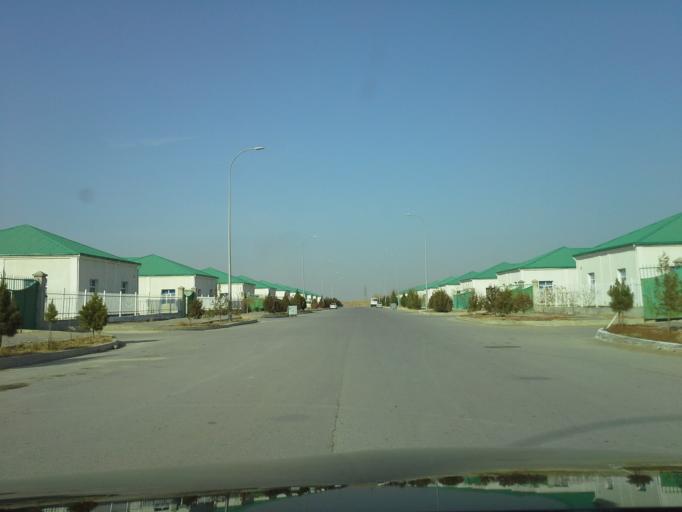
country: TM
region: Ahal
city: Abadan
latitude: 38.1708
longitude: 58.0532
